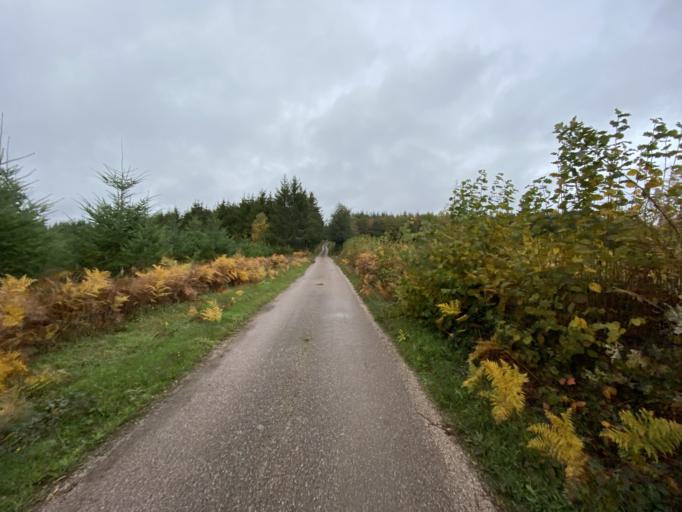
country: FR
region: Bourgogne
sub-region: Departement de la Cote-d'Or
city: Saulieu
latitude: 47.2646
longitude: 4.1667
